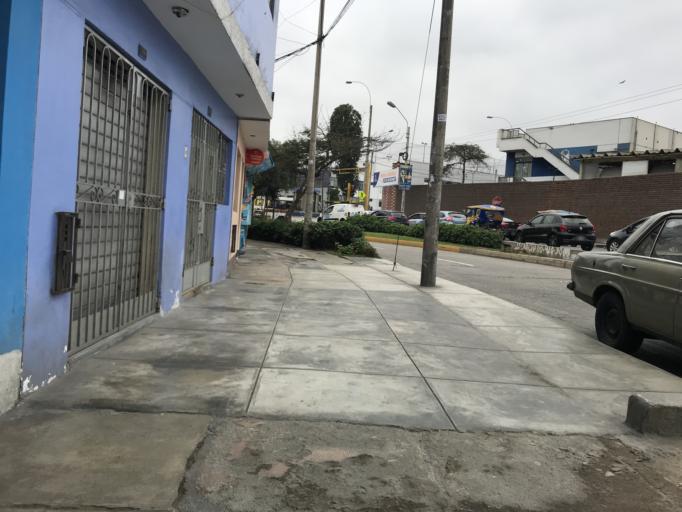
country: PE
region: Lima
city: Lima
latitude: -12.0582
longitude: -77.0674
